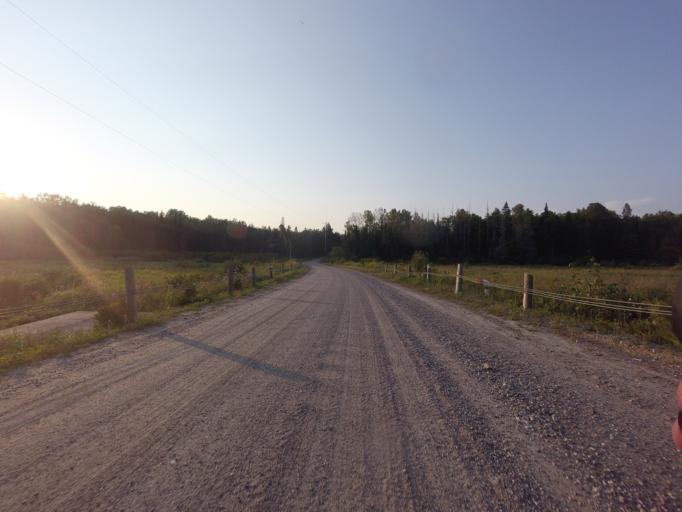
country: CA
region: Ontario
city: Renfrew
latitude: 45.0611
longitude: -76.7539
